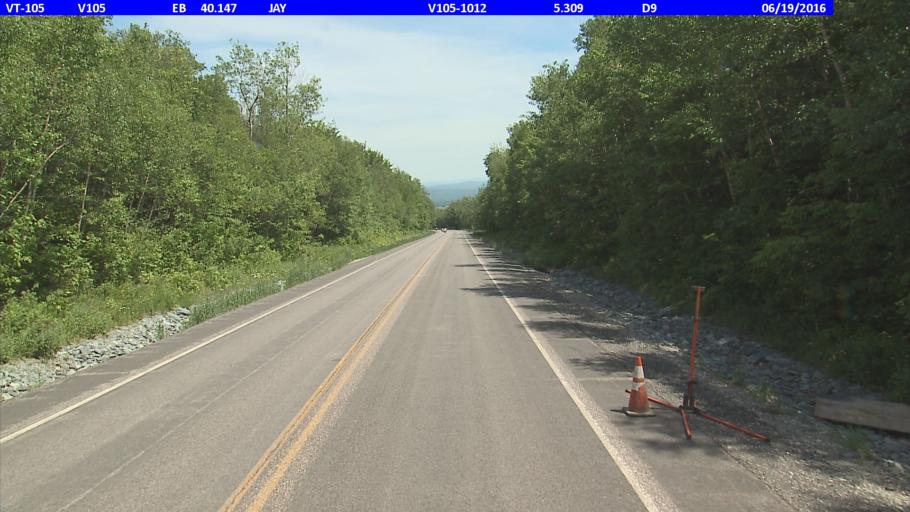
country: CA
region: Quebec
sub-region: Monteregie
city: Sutton
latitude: 44.9783
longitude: -72.4796
